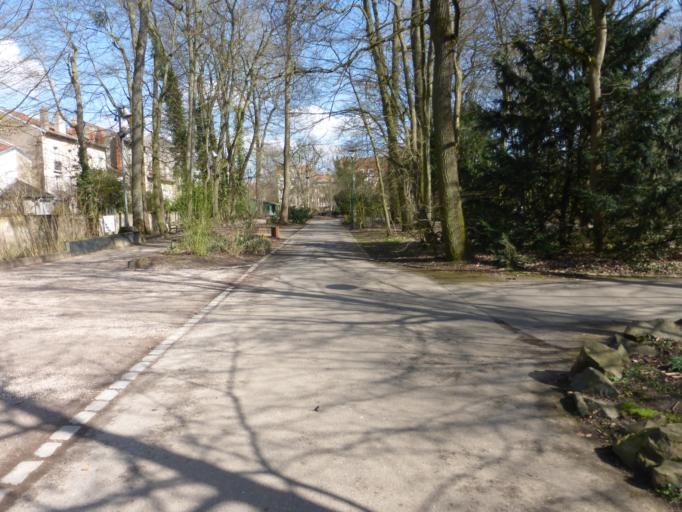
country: FR
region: Lorraine
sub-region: Departement de Meurthe-et-Moselle
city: Nancy
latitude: 48.6815
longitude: 6.1693
